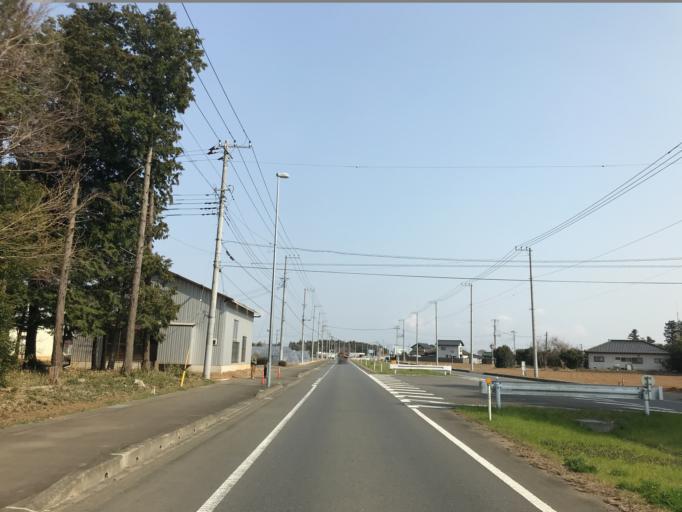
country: JP
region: Ibaraki
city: Okunoya
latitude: 36.1836
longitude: 140.3970
